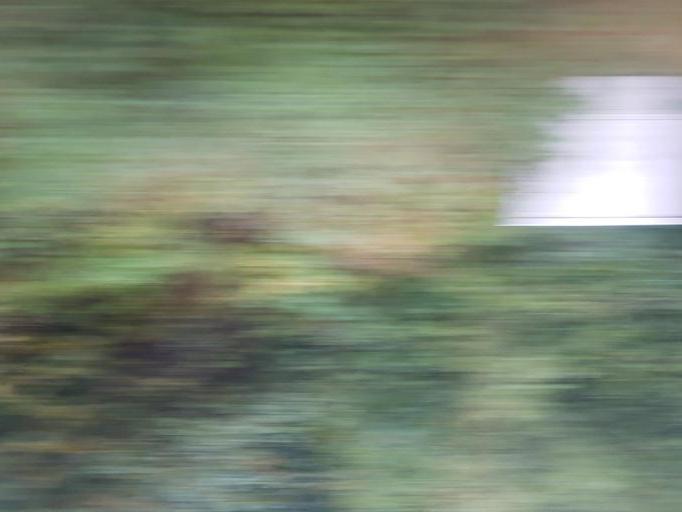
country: NO
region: Sor-Trondelag
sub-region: Melhus
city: Melhus
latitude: 63.2762
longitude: 10.2730
